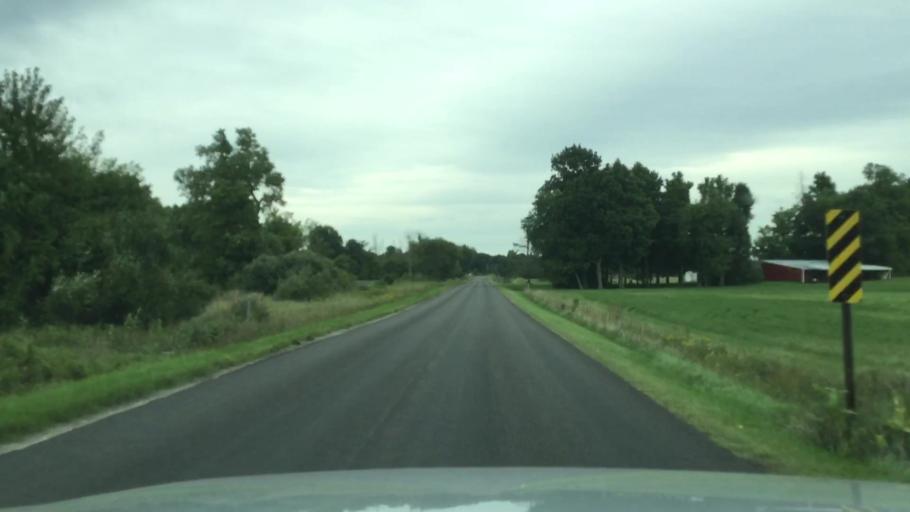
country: US
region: Michigan
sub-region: Shiawassee County
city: Durand
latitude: 42.8663
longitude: -84.0485
